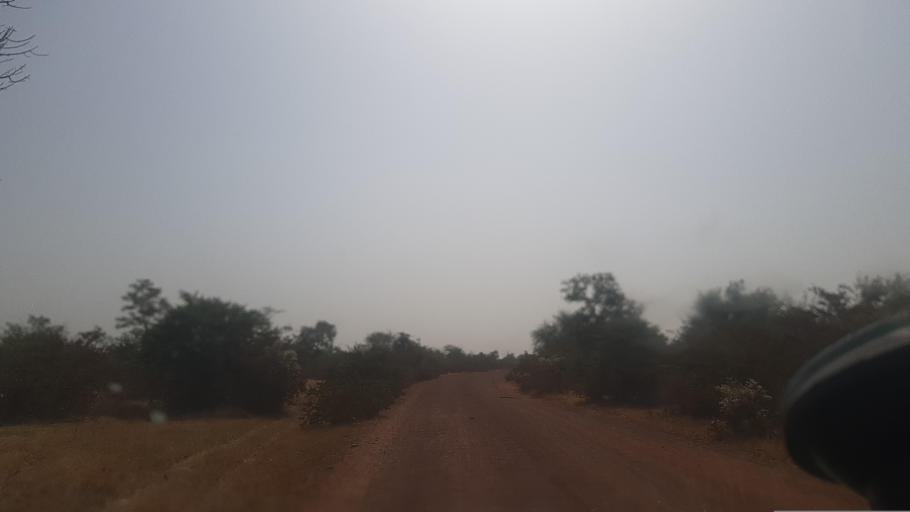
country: ML
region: Segou
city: Baroueli
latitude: 13.0644
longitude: -6.4755
